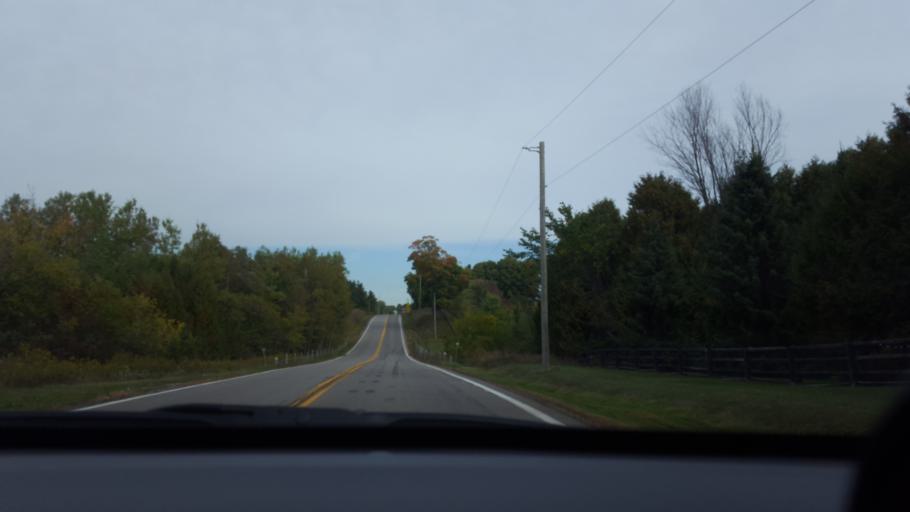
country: CA
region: Ontario
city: Newmarket
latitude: 43.9974
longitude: -79.5466
